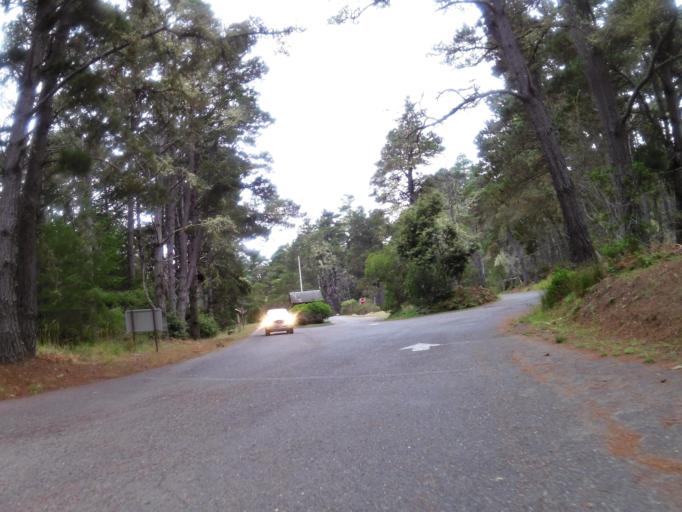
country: US
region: California
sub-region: Sonoma County
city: Sea Ranch
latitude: 38.5697
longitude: -123.3194
